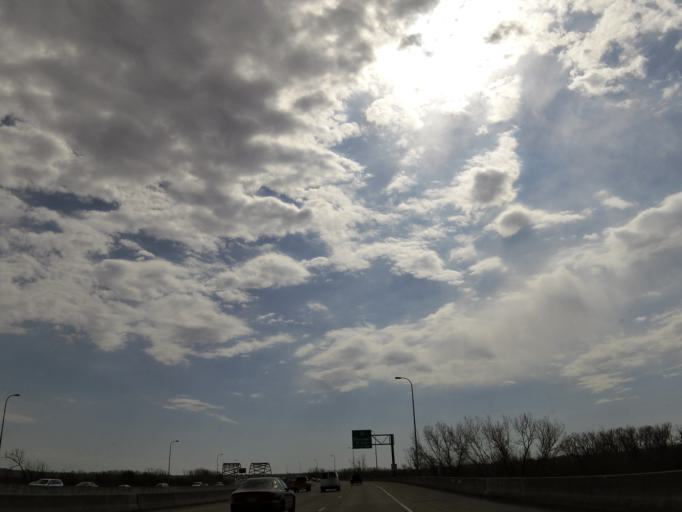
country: US
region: Minnesota
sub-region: Hennepin County
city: Bloomington
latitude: 44.8316
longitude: -93.2370
